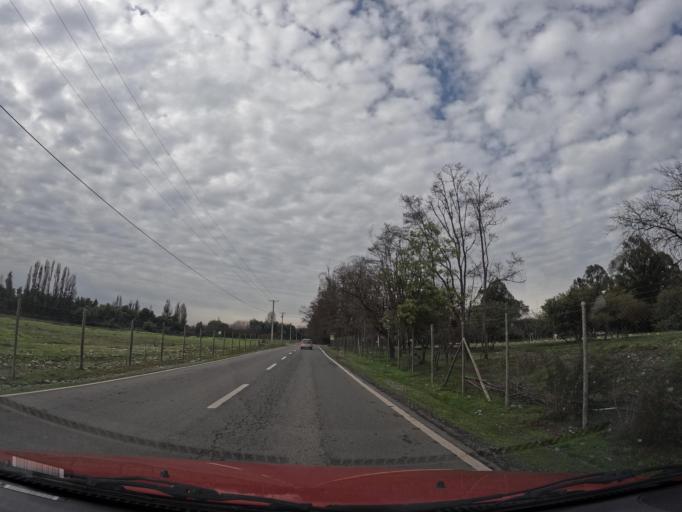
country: CL
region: Maule
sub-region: Provincia de Linares
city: Linares
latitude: -35.8668
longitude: -71.6295
